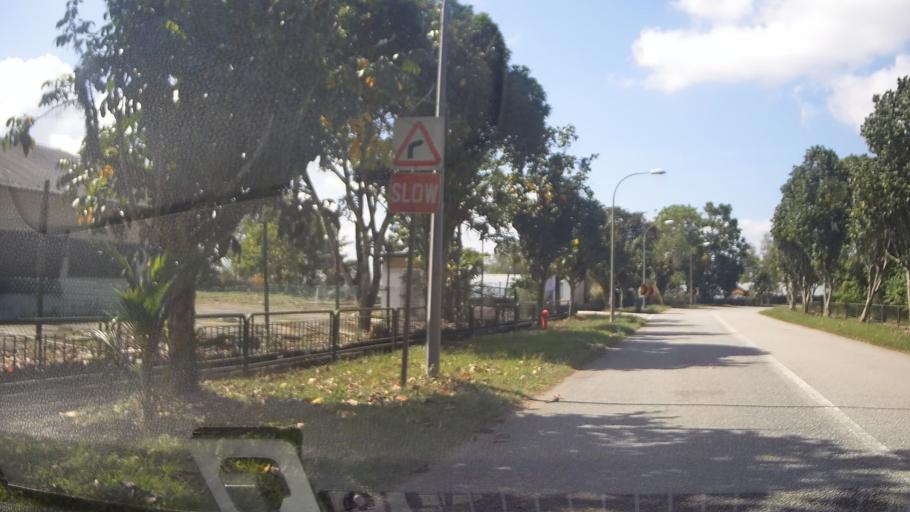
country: MY
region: Johor
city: Johor Bahru
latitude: 1.4336
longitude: 103.7188
